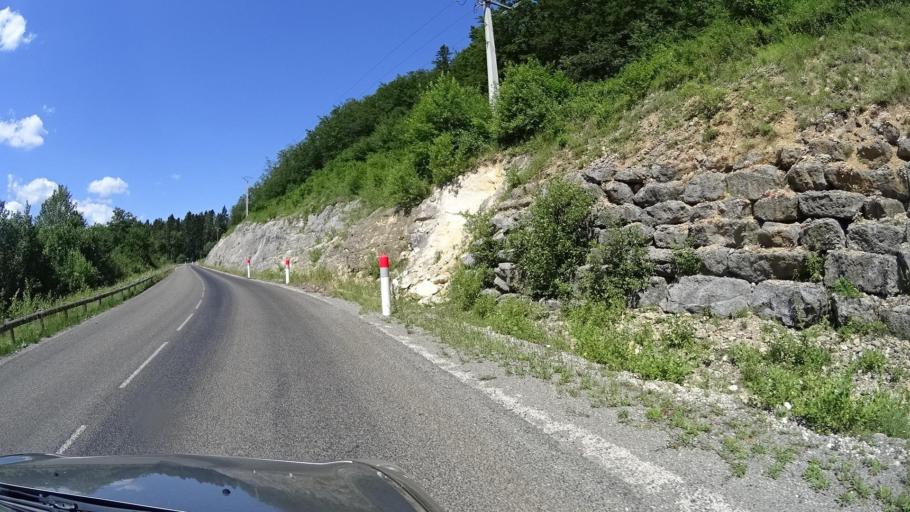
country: FR
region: Franche-Comte
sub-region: Departement du Jura
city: Longchaumois
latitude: 46.5054
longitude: 5.9405
